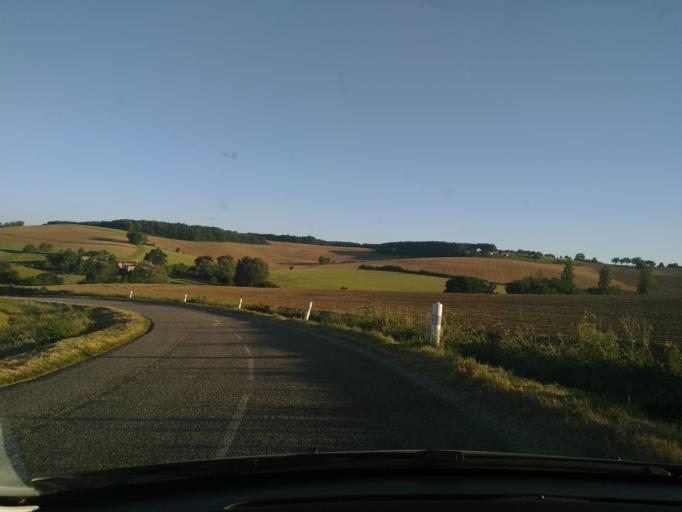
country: FR
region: Midi-Pyrenees
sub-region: Departement du Gers
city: Jegun
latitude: 43.8643
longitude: 0.5072
